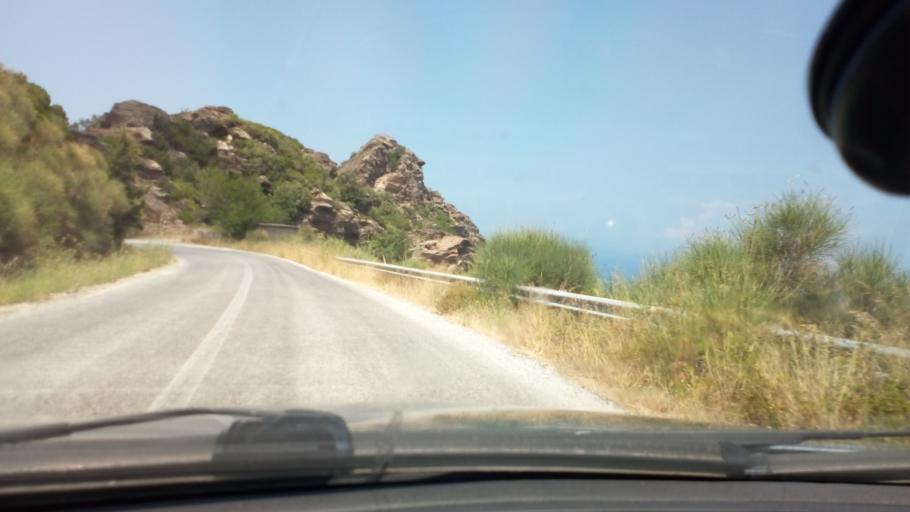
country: GR
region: North Aegean
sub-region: Nomos Samou
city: Agios Kirykos
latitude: 37.6431
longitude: 26.2615
